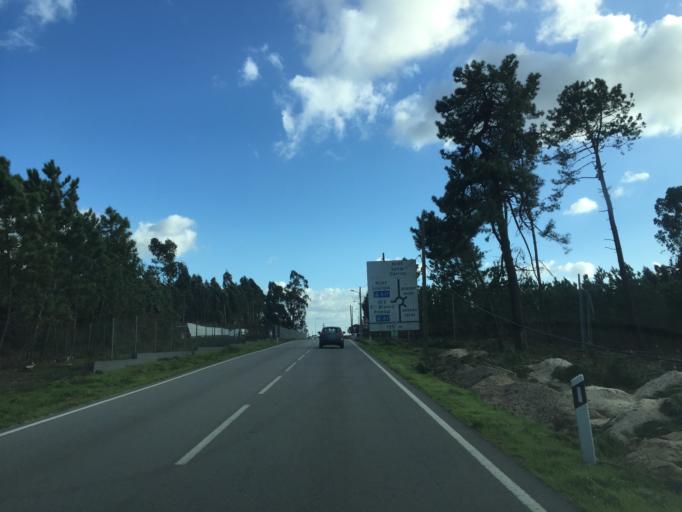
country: PT
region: Leiria
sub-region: Pombal
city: Lourical
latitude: 39.9941
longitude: -8.8035
